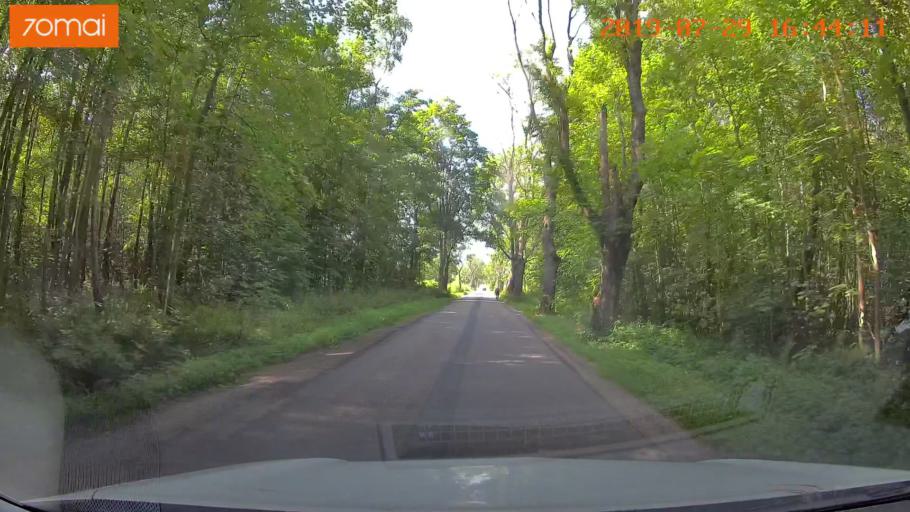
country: RU
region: Kaliningrad
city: Primorsk
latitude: 54.7533
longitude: 20.0892
